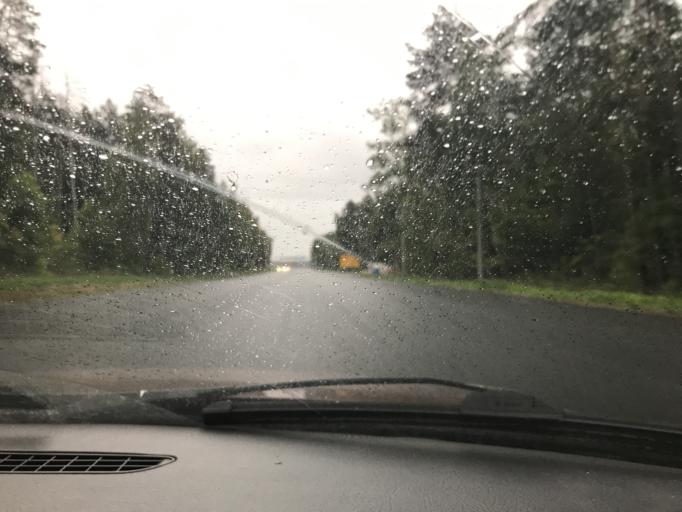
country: RU
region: Kaluga
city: Mstikhino
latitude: 54.5933
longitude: 36.0613
